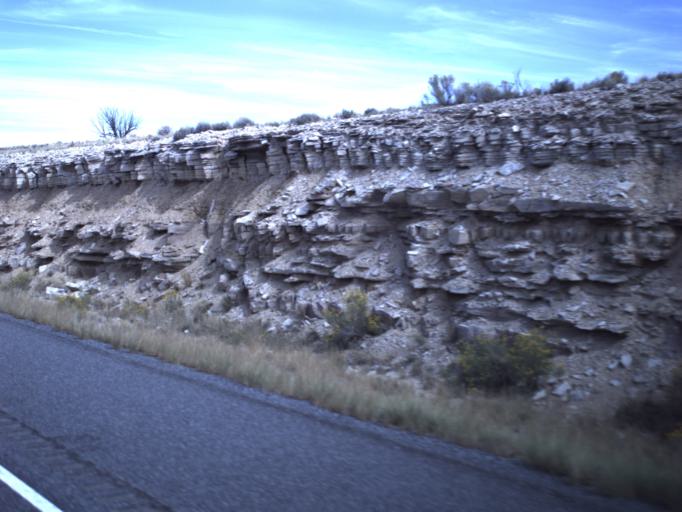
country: US
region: Utah
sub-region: Emery County
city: Castle Dale
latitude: 38.8861
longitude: -110.6510
